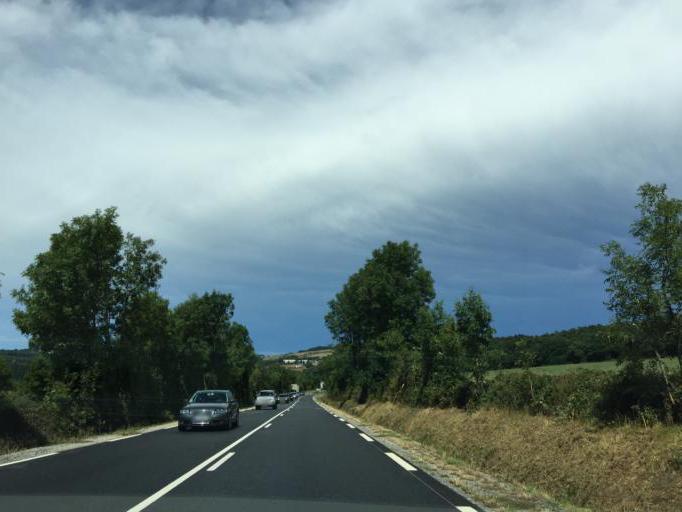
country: FR
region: Midi-Pyrenees
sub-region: Departement de l'Aveyron
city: Severac-le-Chateau
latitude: 44.2276
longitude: 2.9872
